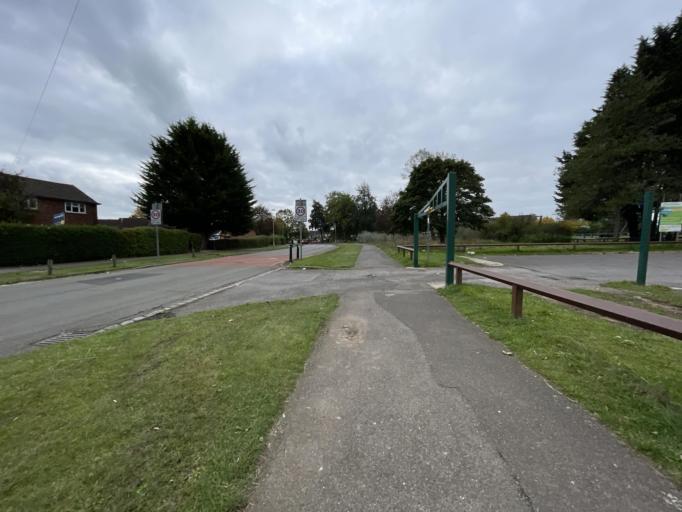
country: GB
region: England
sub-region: West Berkshire
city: Tilehurst
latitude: 51.4544
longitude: -1.0289
